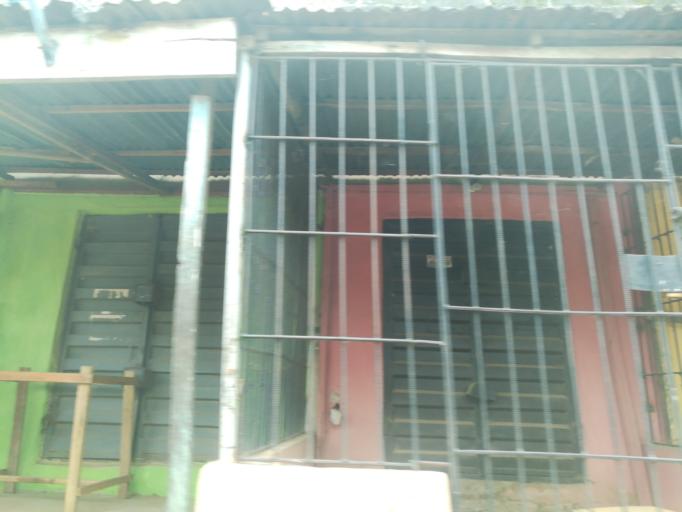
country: NG
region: Lagos
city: Ikorodu
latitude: 6.6137
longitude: 3.5072
